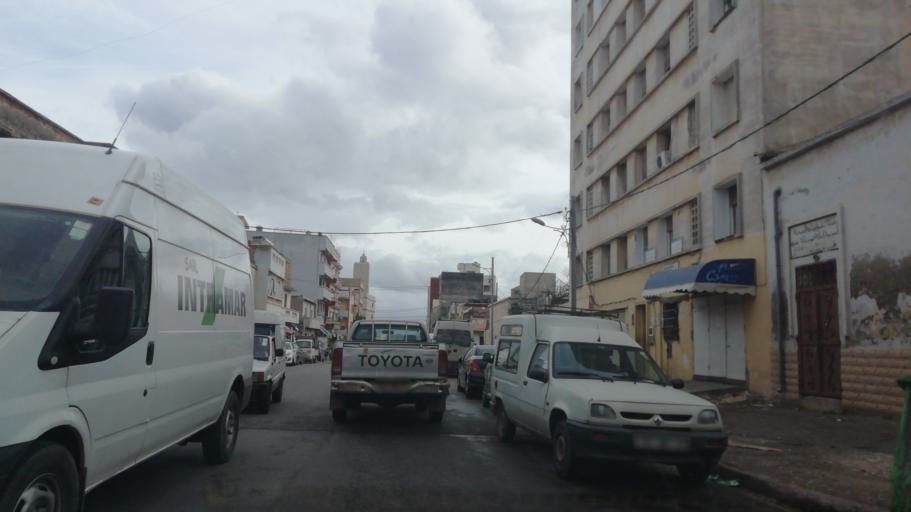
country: DZ
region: Oran
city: Oran
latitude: 35.6856
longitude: -0.6432
